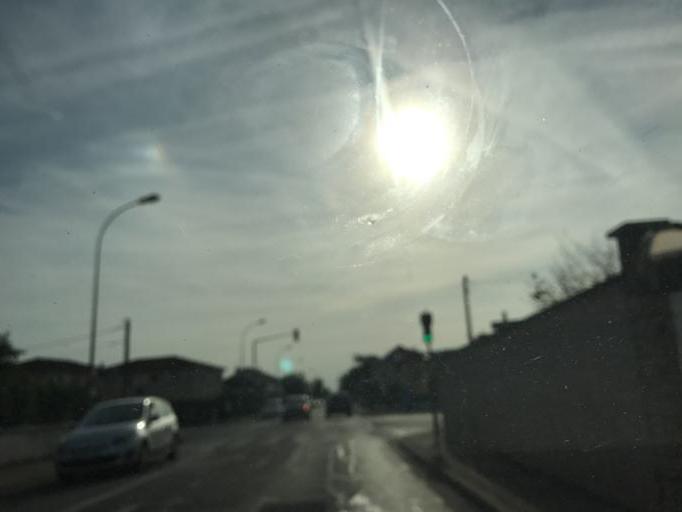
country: FR
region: Rhone-Alpes
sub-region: Departement du Rhone
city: Meyzieu
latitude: 45.7797
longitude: 4.9974
